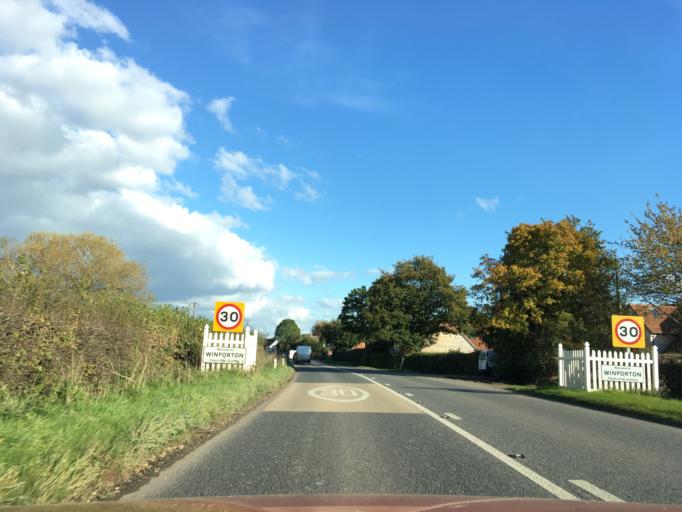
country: GB
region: England
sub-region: Herefordshire
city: Dorstone
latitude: 52.1170
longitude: -3.0341
